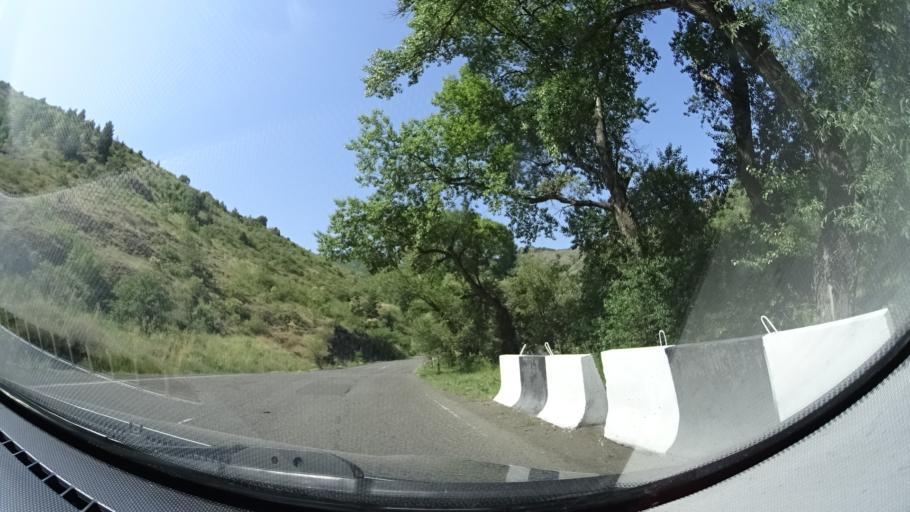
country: GE
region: Samtskhe-Javakheti
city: Akhaltsikhe
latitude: 41.6194
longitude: 43.0688
